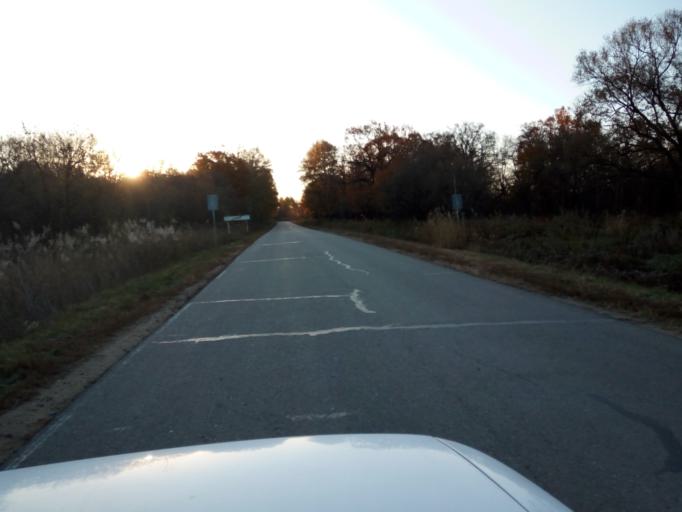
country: RU
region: Primorskiy
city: Lazo
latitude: 45.8718
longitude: 133.6568
